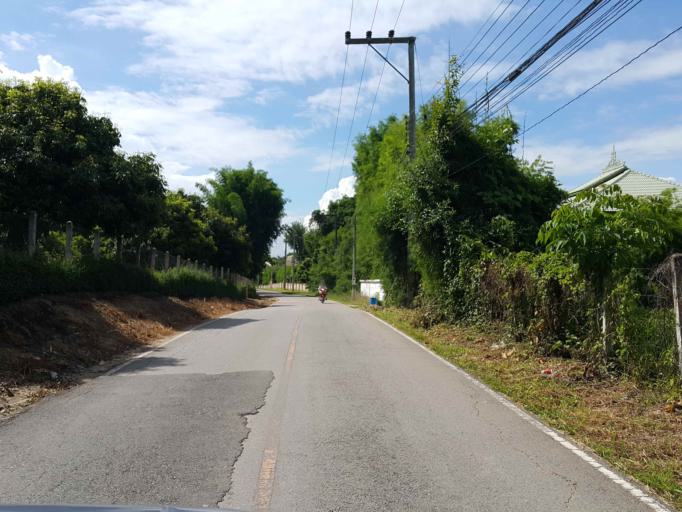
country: TH
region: Chiang Mai
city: Mae Taeng
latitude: 18.9640
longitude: 98.9129
